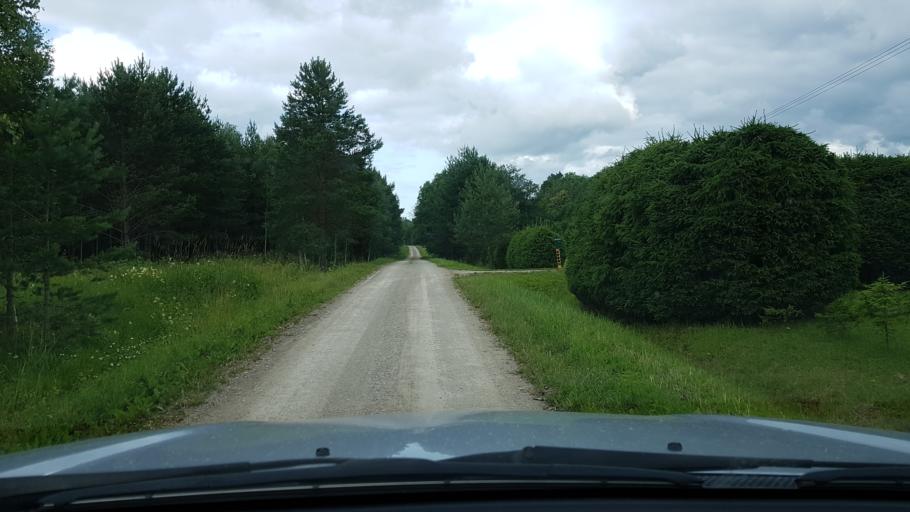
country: EE
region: Ida-Virumaa
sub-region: Narva-Joesuu linn
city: Narva-Joesuu
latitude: 59.4065
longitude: 27.9761
